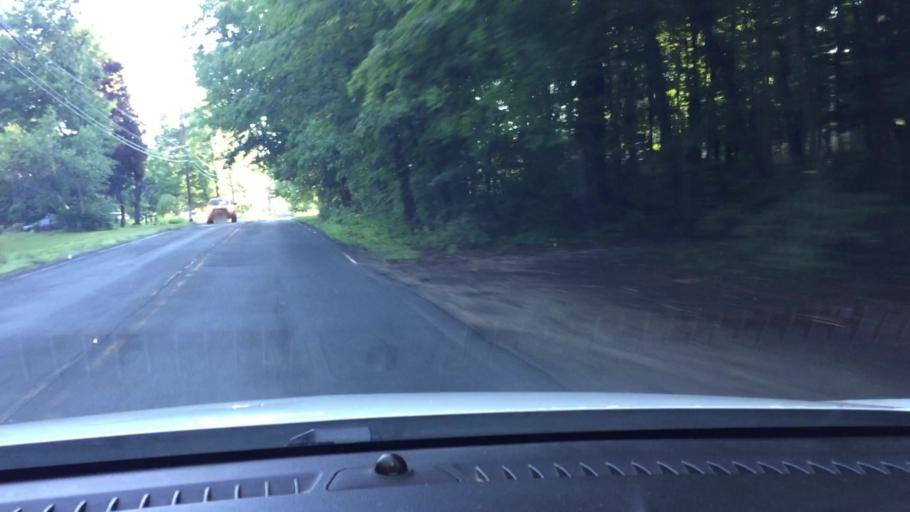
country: US
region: Massachusetts
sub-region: Berkshire County
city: Pittsfield
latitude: 42.4277
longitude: -73.2258
